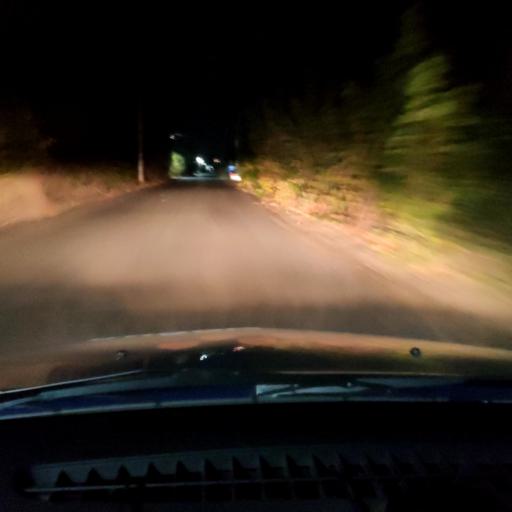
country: RU
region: Voronezj
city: Shilovo
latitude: 51.5917
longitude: 39.1587
